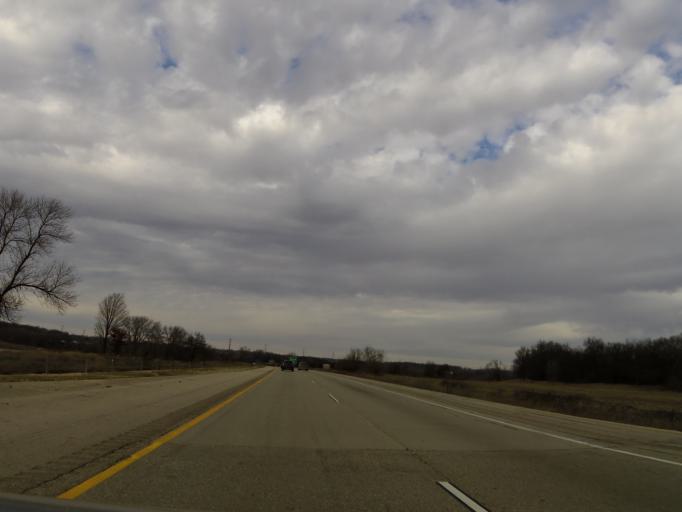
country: US
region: Wisconsin
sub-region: Rock County
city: Edgerton
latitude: 42.8553
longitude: -89.0362
